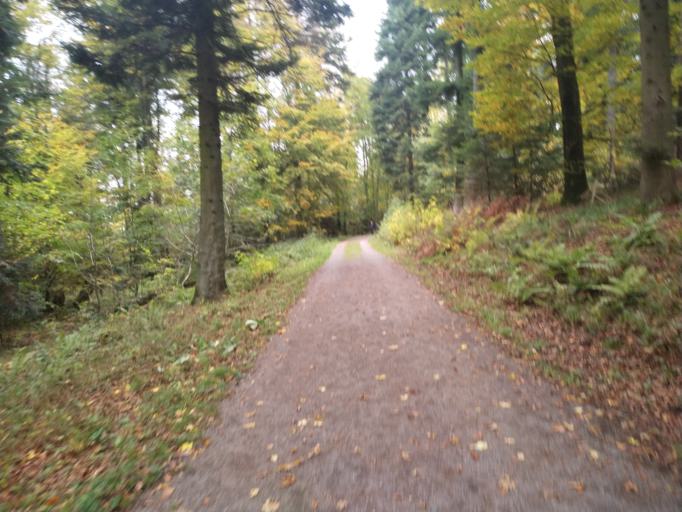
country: DE
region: Baden-Wuerttemberg
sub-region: Karlsruhe Region
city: Birkenfeld
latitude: 48.8583
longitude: 8.6457
